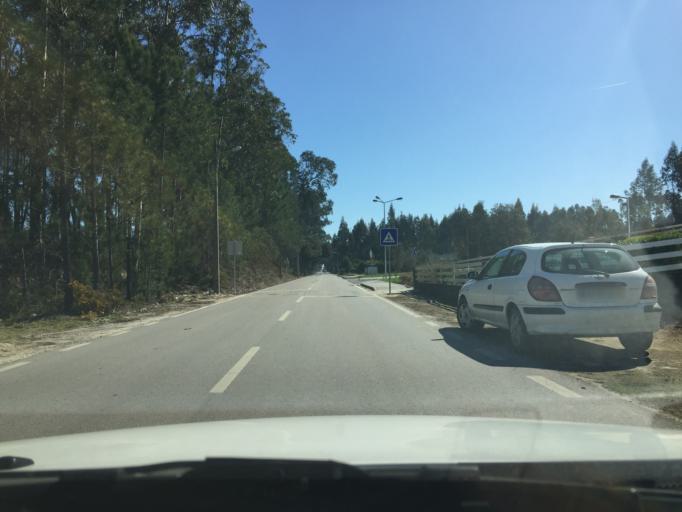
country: PT
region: Coimbra
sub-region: Cantanhede
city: Cantanhede
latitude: 40.4189
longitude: -8.5551
